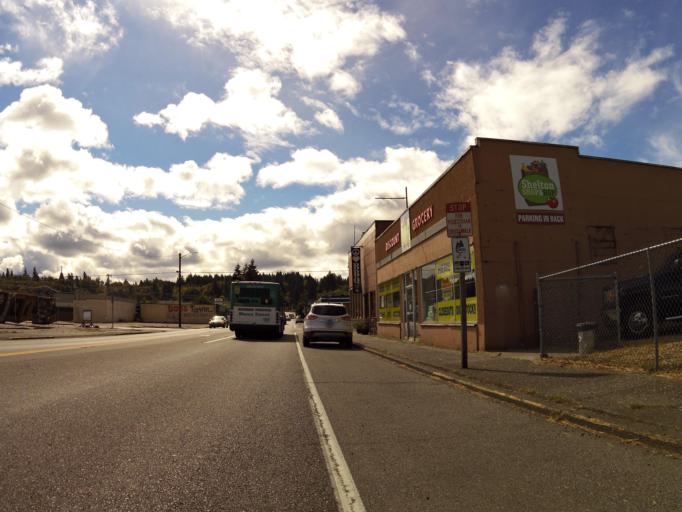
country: US
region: Washington
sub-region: Mason County
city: Shelton
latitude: 47.2117
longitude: -123.1003
